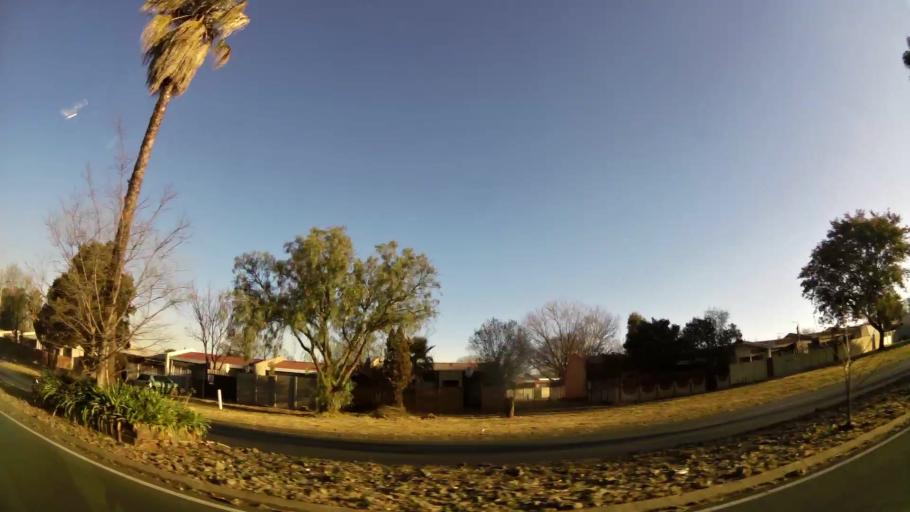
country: ZA
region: Gauteng
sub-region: City of Johannesburg Metropolitan Municipality
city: Roodepoort
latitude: -26.1810
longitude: 27.9036
